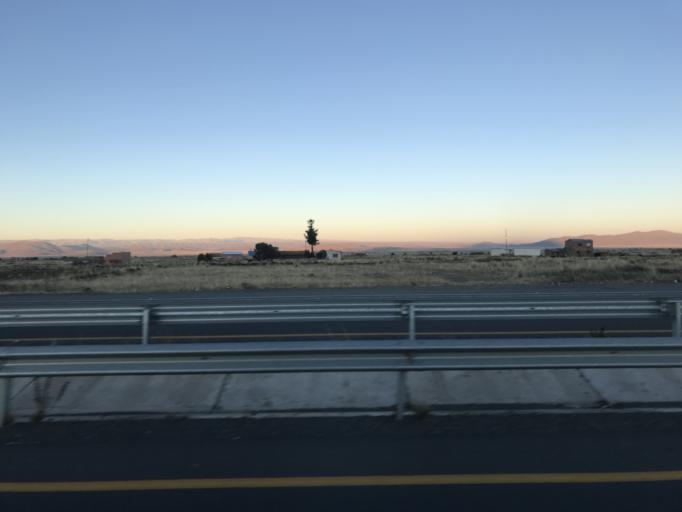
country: BO
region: La Paz
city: Batallas
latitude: -16.3537
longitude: -68.4003
